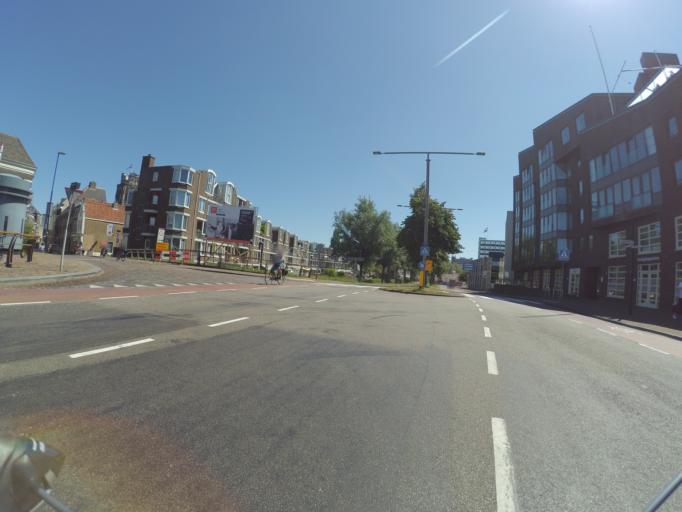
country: NL
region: South Holland
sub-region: Gemeente Dordrecht
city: Dordrecht
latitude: 51.8121
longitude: 4.6582
